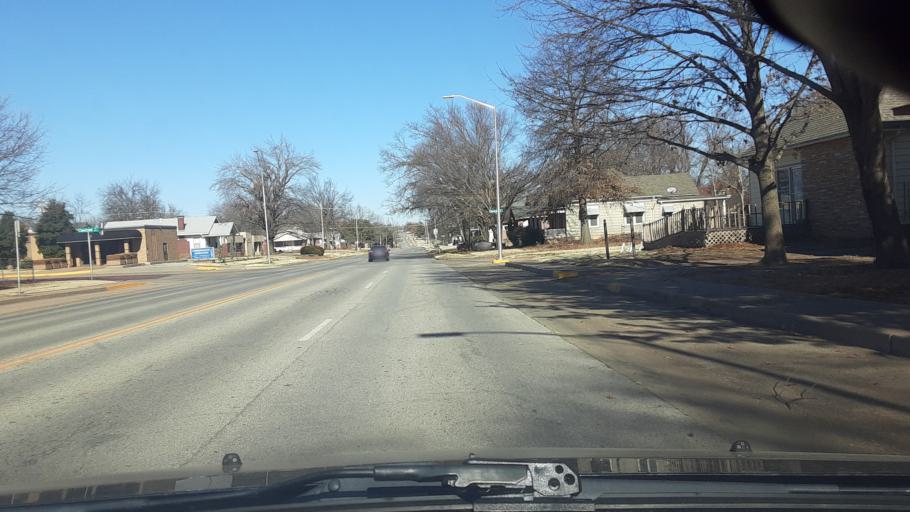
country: US
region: Oklahoma
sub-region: Kay County
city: Ponca City
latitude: 36.7052
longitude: -97.0785
